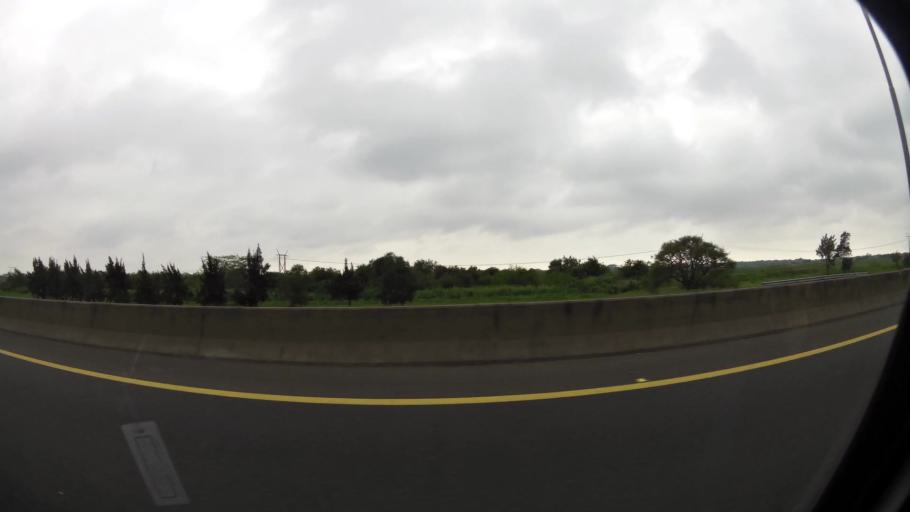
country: AR
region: Buenos Aires
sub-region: Partido de Quilmes
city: Quilmes
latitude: -34.7233
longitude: -58.2270
